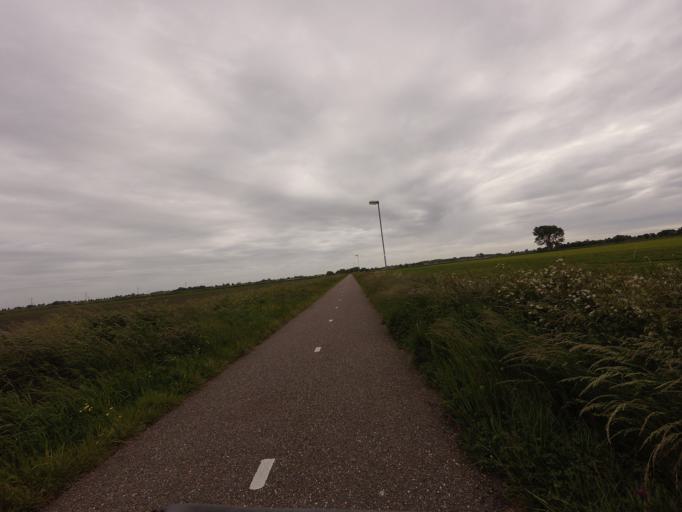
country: NL
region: North Holland
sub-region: Gemeente Medemblik
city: Opperdoes
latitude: 52.7098
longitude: 5.0713
